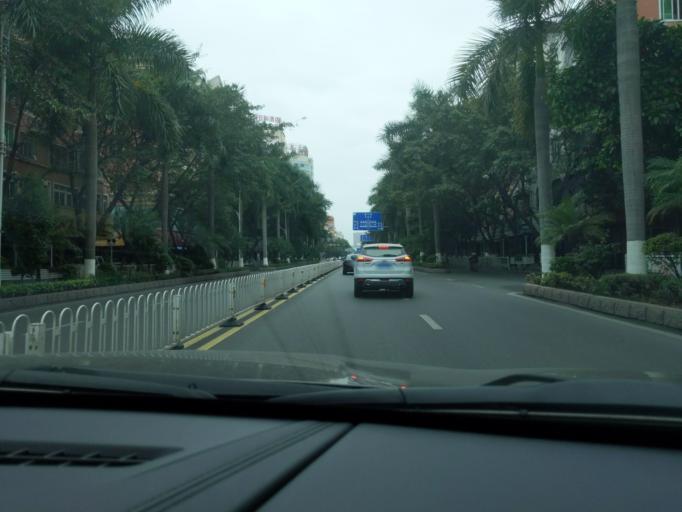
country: CN
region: Fujian
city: Shishi
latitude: 24.7370
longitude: 118.6402
